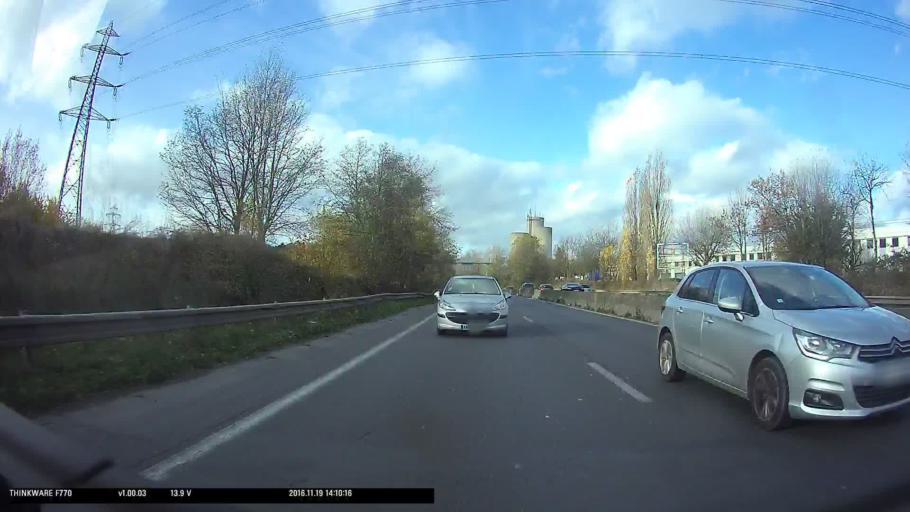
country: FR
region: Ile-de-France
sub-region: Departement du Val-d'Oise
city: Osny
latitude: 49.0492
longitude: 2.0697
